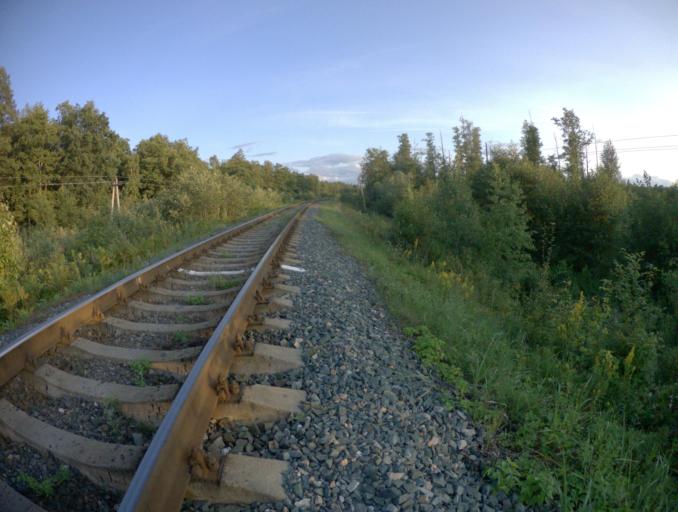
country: RU
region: Vladimir
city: Raduzhnyy
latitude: 56.0407
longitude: 40.3849
